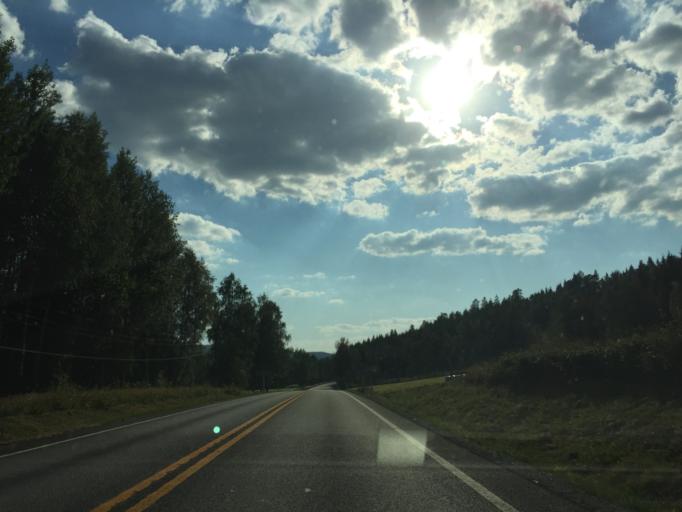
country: NO
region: Hedmark
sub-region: Kongsvinger
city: Spetalen
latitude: 60.2123
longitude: 11.9136
